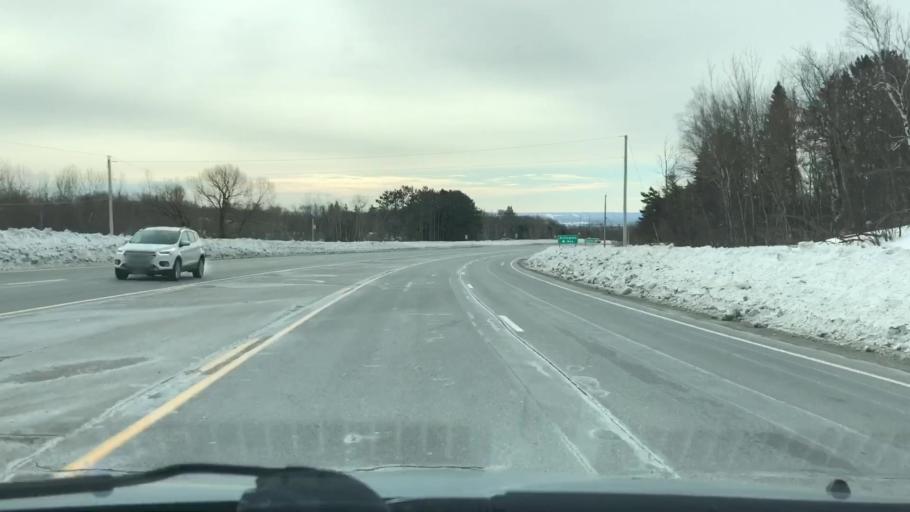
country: US
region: Minnesota
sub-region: Saint Louis County
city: Duluth
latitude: 46.7854
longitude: -92.1404
